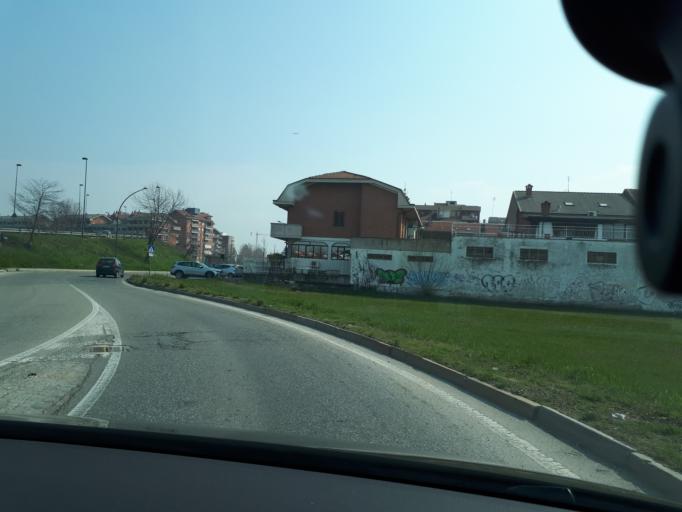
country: IT
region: Piedmont
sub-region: Provincia di Torino
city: Lesna
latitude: 45.0642
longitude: 7.6044
